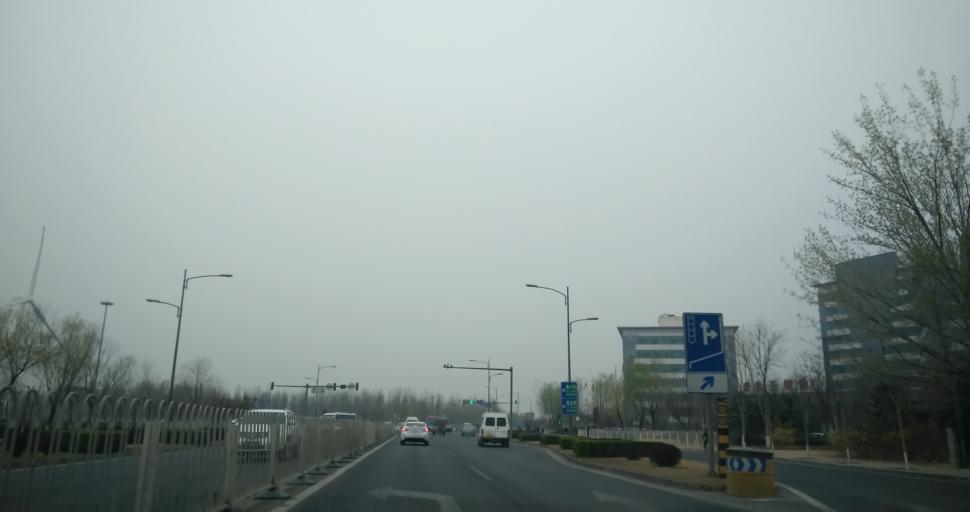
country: CN
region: Beijing
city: Jiugong
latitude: 39.7657
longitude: 116.5234
